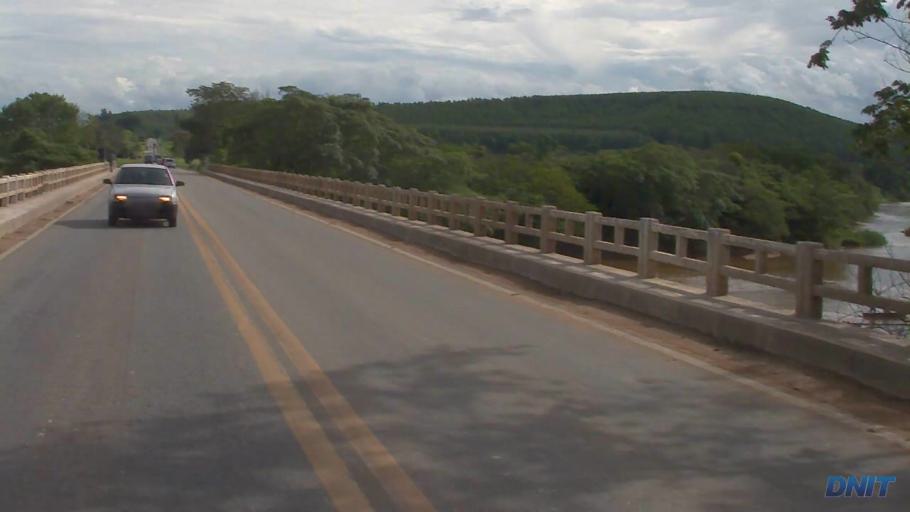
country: BR
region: Minas Gerais
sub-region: Belo Oriente
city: Belo Oriente
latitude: -19.2369
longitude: -42.3316
